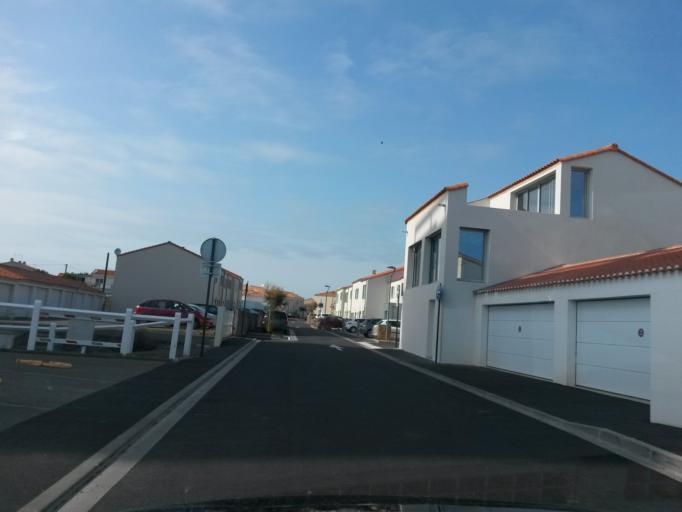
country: FR
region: Pays de la Loire
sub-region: Departement de la Vendee
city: Les Sables-d'Olonne
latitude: 46.4897
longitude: -1.7968
